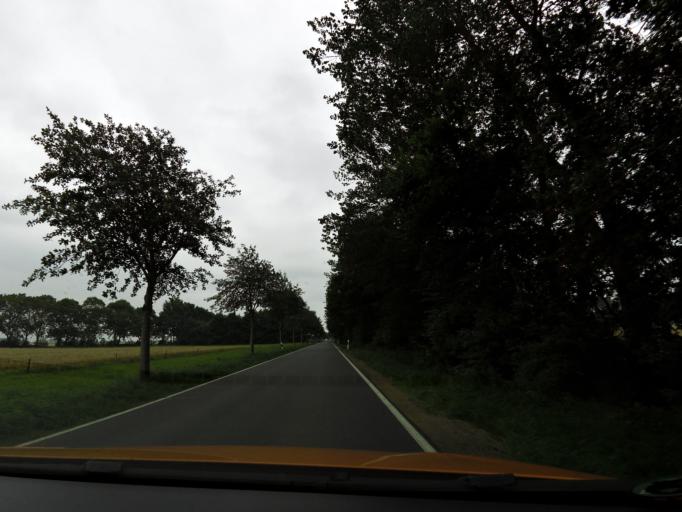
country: DE
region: Lower Saxony
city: Wirdum
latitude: 53.5110
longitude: 7.1452
